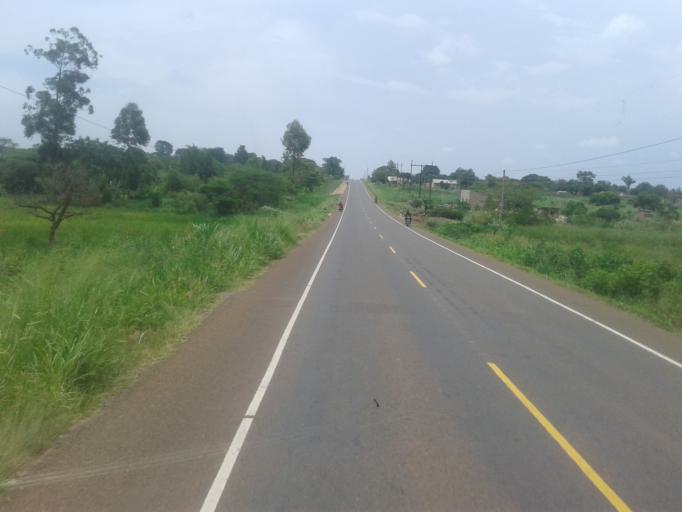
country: UG
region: Western Region
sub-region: Kiryandongo District
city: Kiryandongo
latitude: 1.8817
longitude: 32.0655
